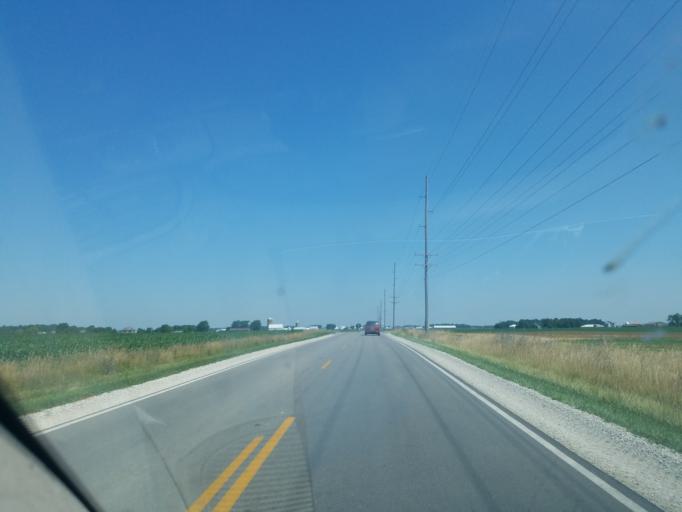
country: US
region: Ohio
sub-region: Mercer County
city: Saint Henry
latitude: 40.4443
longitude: -84.6482
